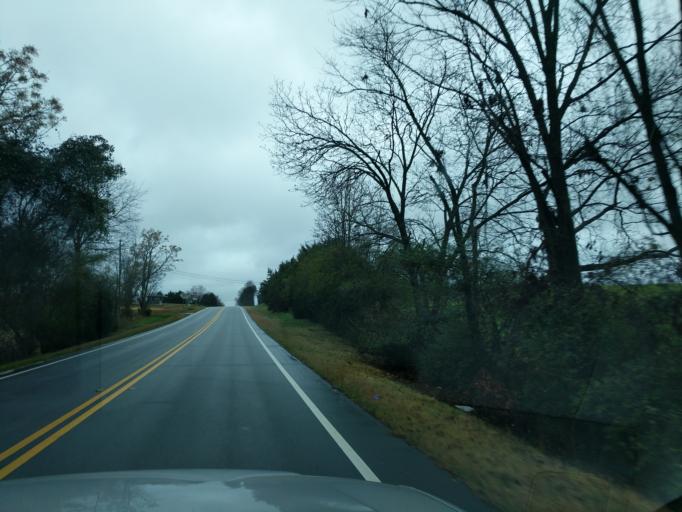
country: US
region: Georgia
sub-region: Franklin County
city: Lavonia
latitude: 34.3623
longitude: -83.0952
